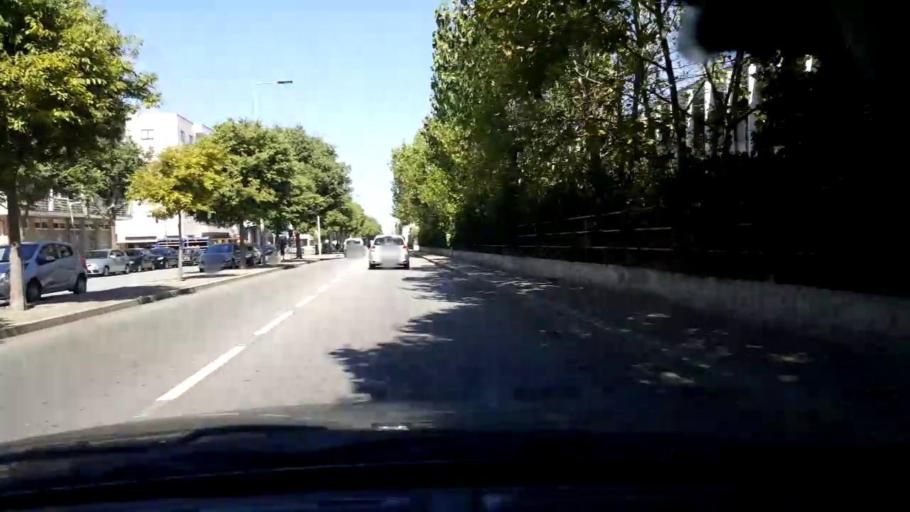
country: PT
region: Porto
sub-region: Povoa de Varzim
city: Povoa de Varzim
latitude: 41.3715
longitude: -8.7537
